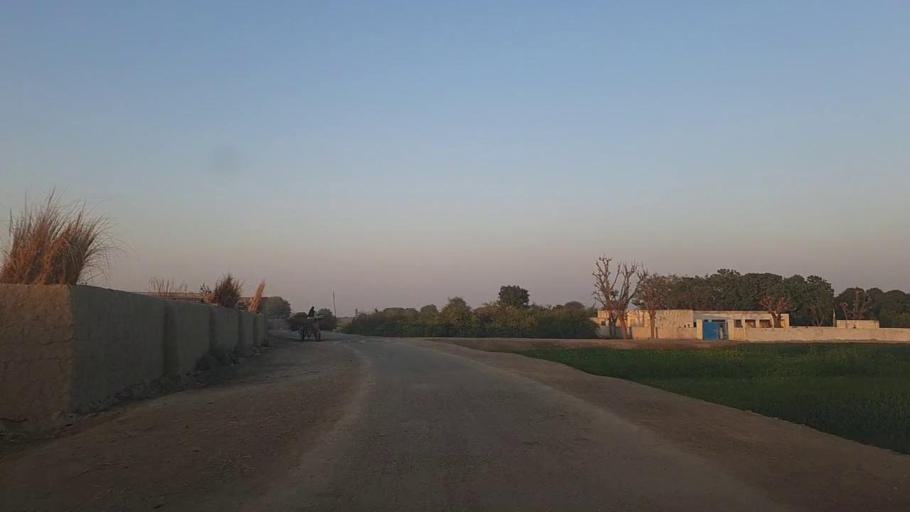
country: PK
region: Sindh
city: Jam Sahib
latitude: 26.3707
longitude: 68.7230
